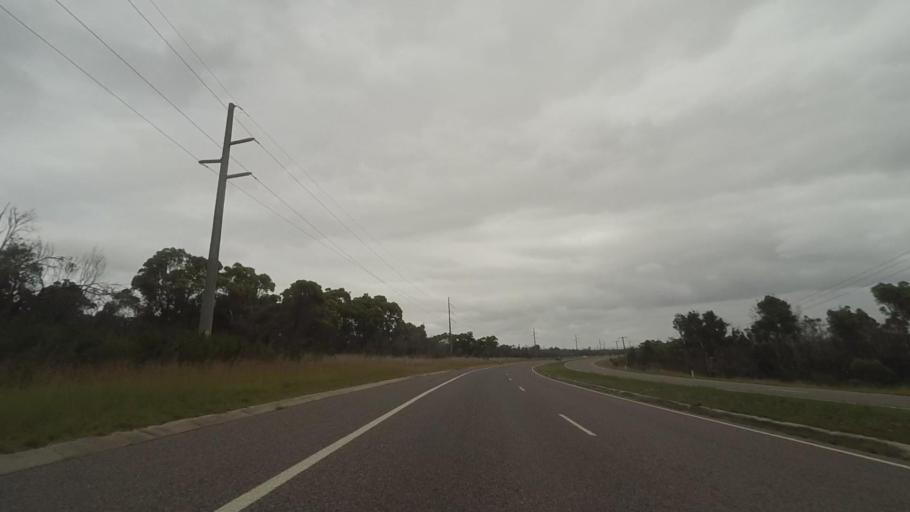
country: AU
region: New South Wales
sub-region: Wyong Shire
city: Kingfisher Shores
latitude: -33.1844
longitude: 151.5906
